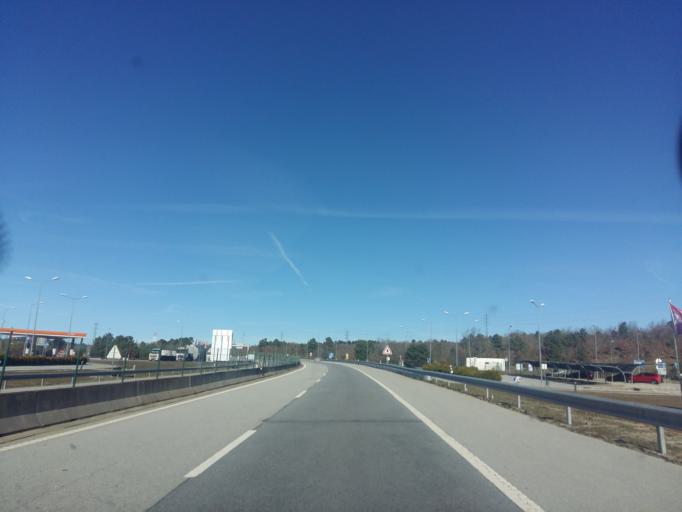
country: PT
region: Guarda
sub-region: Guarda
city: Sequeira
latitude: 40.5433
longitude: -7.2160
